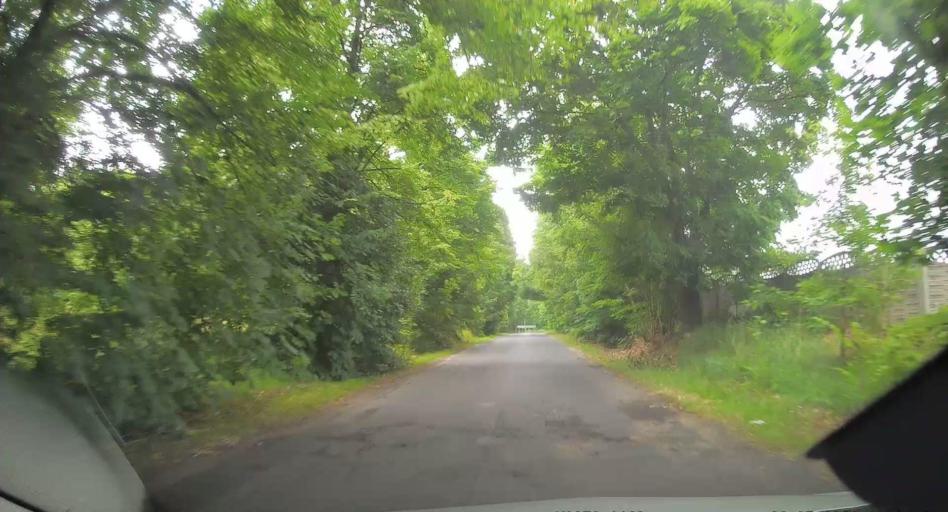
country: PL
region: Lodz Voivodeship
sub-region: Powiat rawski
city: Rawa Mazowiecka
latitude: 51.7436
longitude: 20.1864
